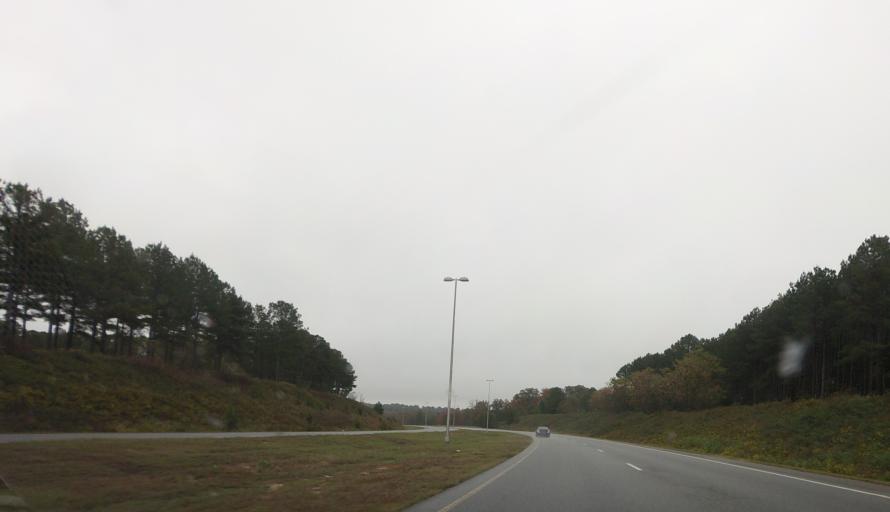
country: US
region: Georgia
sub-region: Houston County
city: Centerville
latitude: 32.5815
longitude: -83.6881
